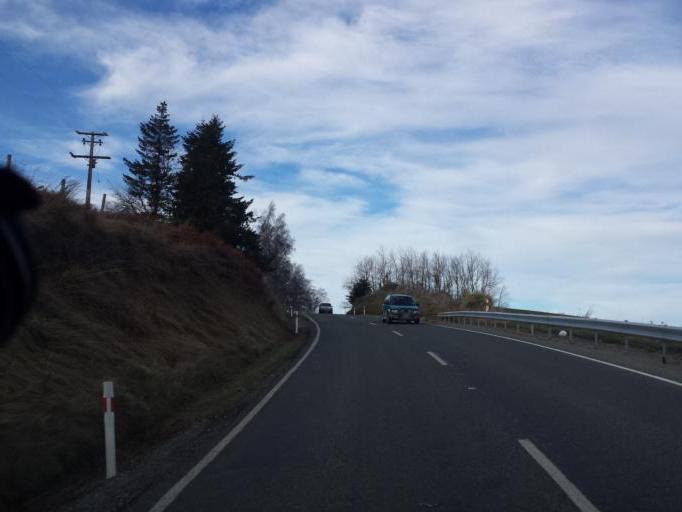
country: NZ
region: Canterbury
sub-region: Timaru District
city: Pleasant Point
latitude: -44.0962
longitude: 170.9993
